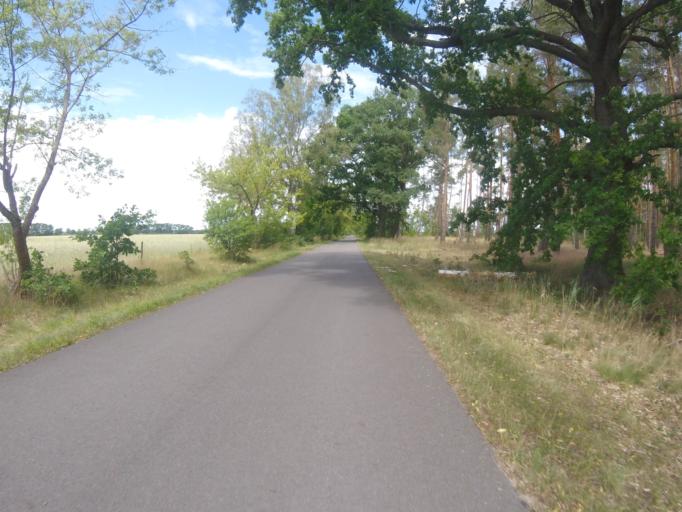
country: DE
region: Brandenburg
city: Bestensee
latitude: 52.2265
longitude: 13.7063
